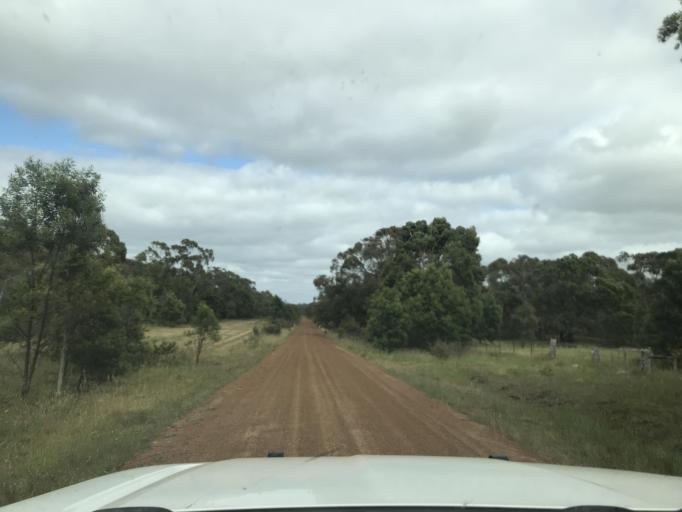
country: AU
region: South Australia
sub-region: Wattle Range
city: Penola
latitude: -37.3344
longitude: 141.4219
